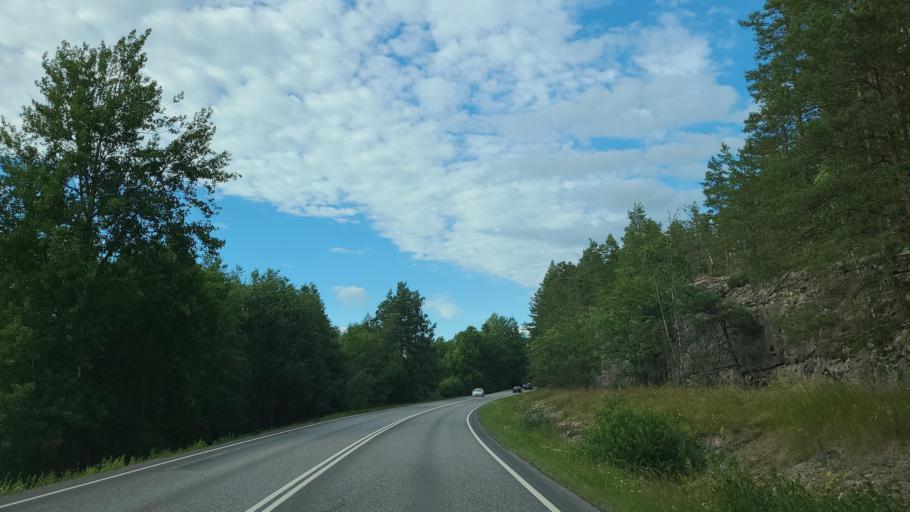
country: FI
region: Varsinais-Suomi
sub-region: Turku
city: Merimasku
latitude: 60.4459
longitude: 21.8972
